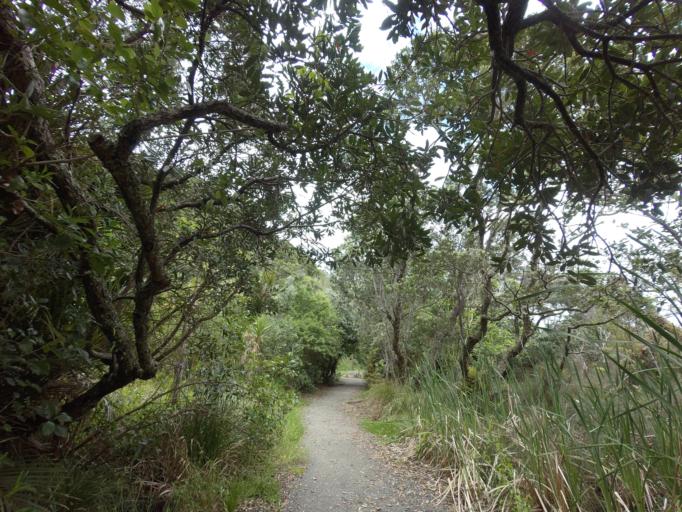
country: NZ
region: Auckland
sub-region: Auckland
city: Warkworth
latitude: -36.5341
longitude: 174.7099
